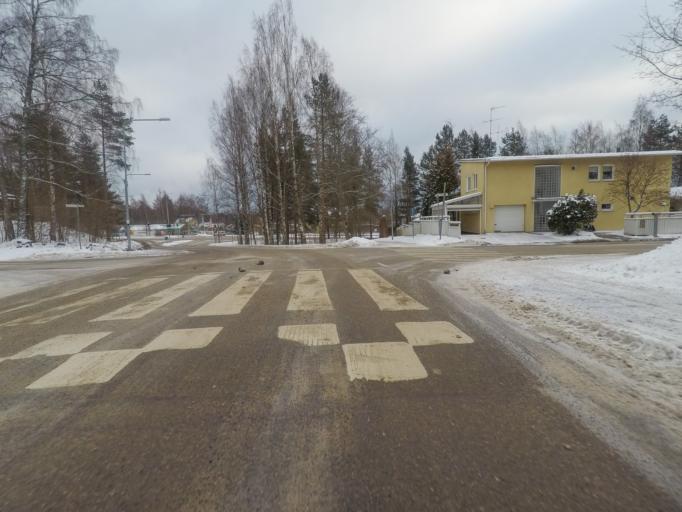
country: FI
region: Uusimaa
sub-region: Helsinki
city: Vantaa
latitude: 60.2217
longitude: 25.1076
